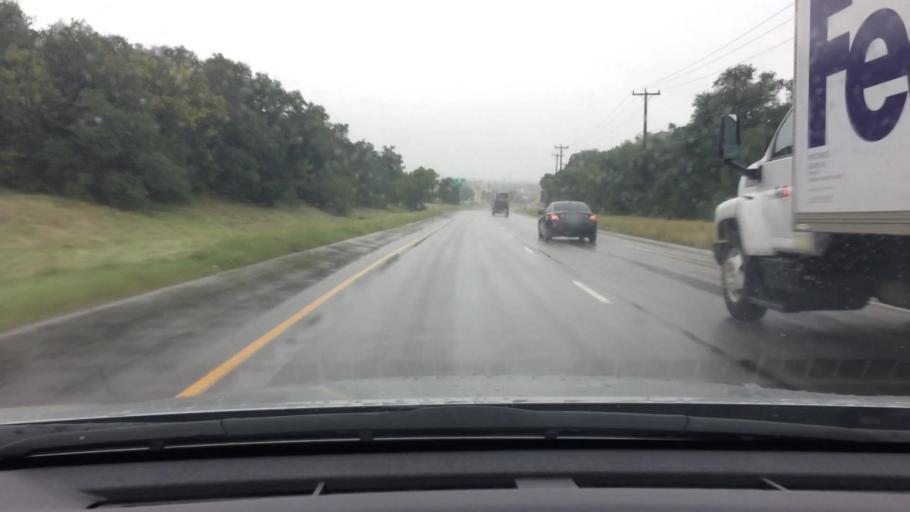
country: US
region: Texas
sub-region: Bexar County
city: Leon Valley
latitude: 29.4850
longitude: -98.7080
